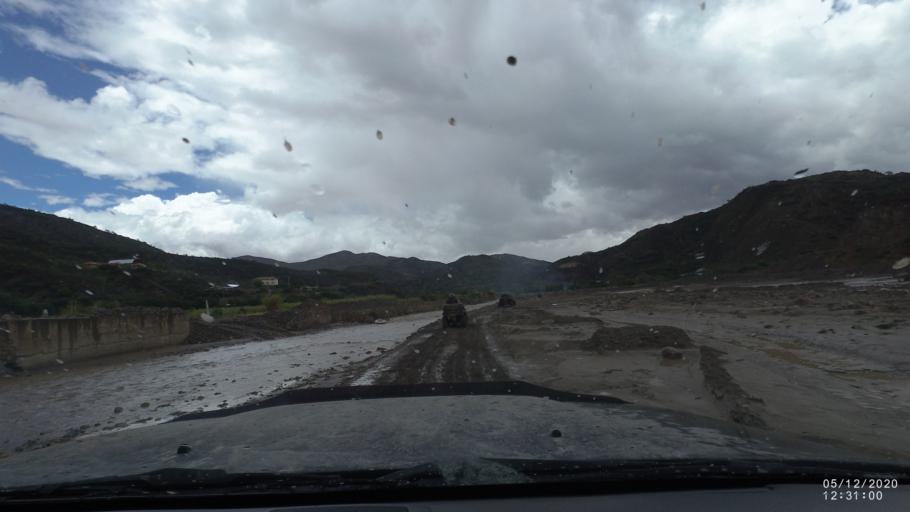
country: BO
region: Cochabamba
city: Sipe Sipe
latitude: -17.5456
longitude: -66.4189
